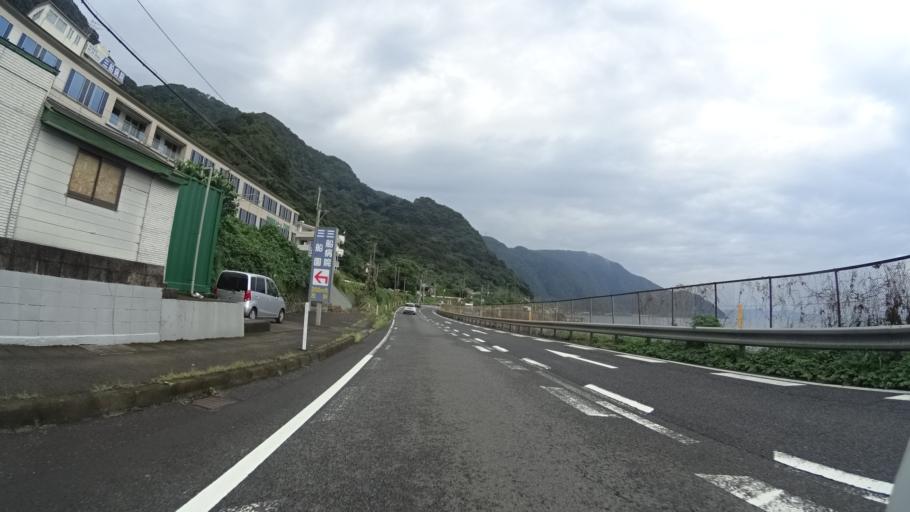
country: JP
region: Kagoshima
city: Kagoshima-shi
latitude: 31.6329
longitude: 130.6019
